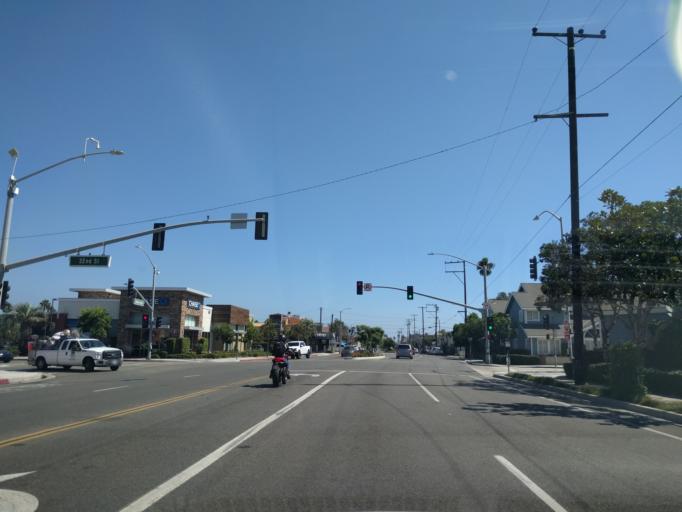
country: US
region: California
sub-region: Orange County
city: Newport Beach
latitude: 33.6150
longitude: -117.9329
